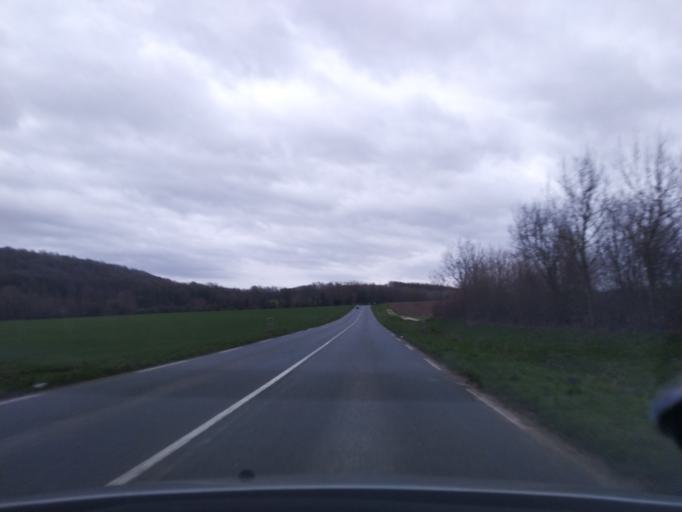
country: FR
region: Nord-Pas-de-Calais
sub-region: Departement du Pas-de-Calais
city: Calonne-Ricouart
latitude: 50.4498
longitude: 2.4707
